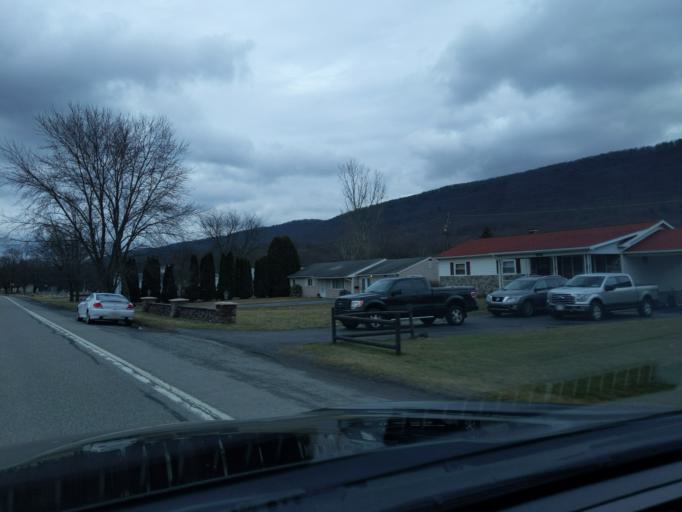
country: US
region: Pennsylvania
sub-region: Blair County
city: Tipton
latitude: 40.6346
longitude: -78.2858
